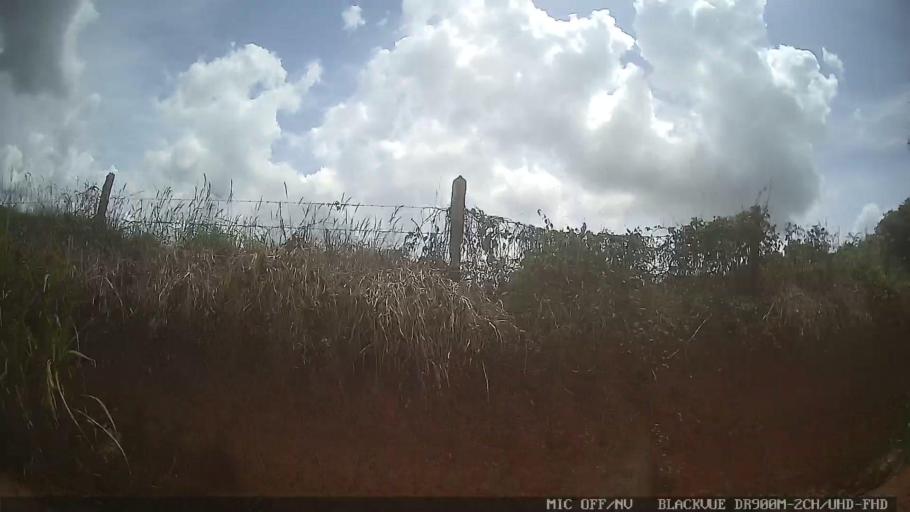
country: BR
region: Sao Paulo
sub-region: Atibaia
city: Atibaia
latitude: -23.0434
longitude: -46.5197
